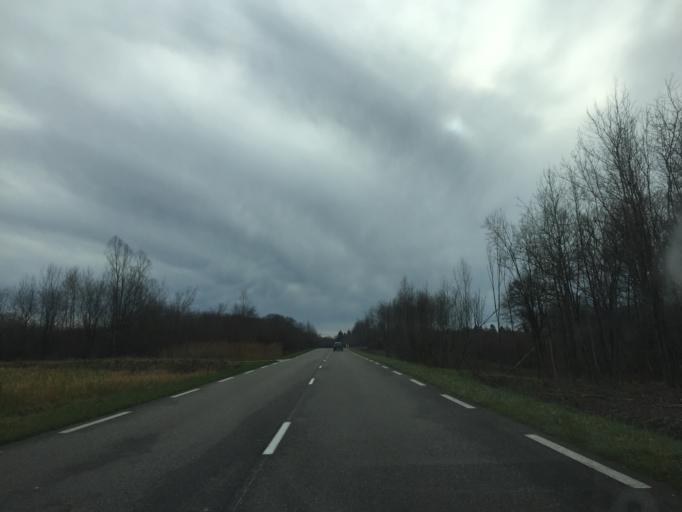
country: FR
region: Franche-Comte
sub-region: Departement du Jura
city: Mont-sous-Vaudrey
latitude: 46.8882
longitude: 5.5262
